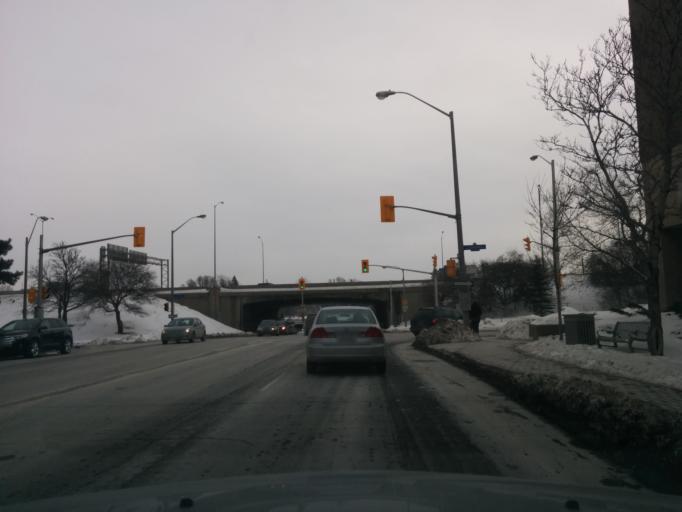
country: CA
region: Ontario
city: Ottawa
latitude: 45.4126
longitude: -75.6859
